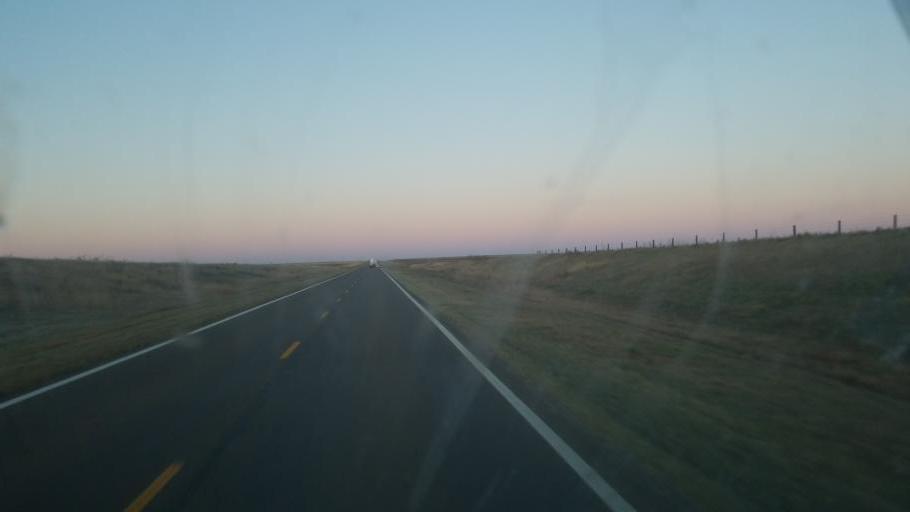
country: US
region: Kansas
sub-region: Wallace County
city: Sharon Springs
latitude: 38.9050
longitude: -101.6325
